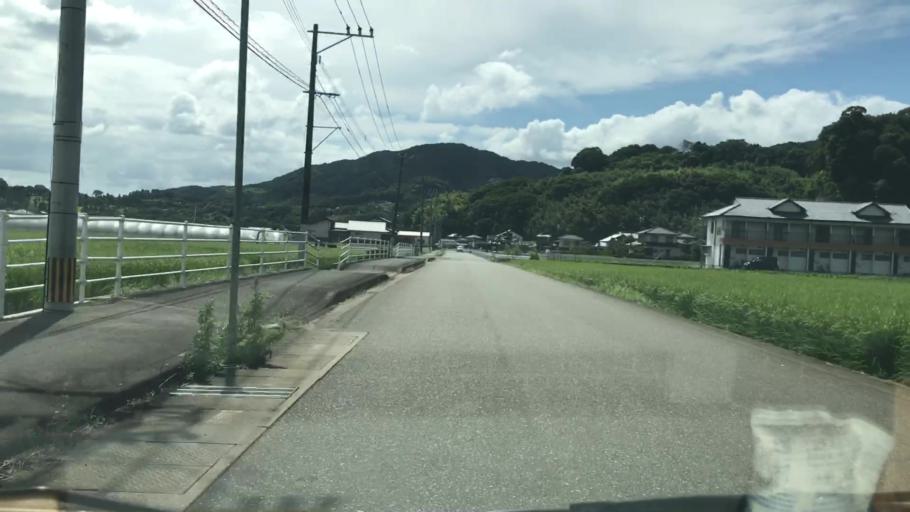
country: JP
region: Saga Prefecture
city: Saga-shi
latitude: 33.2379
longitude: 130.1819
